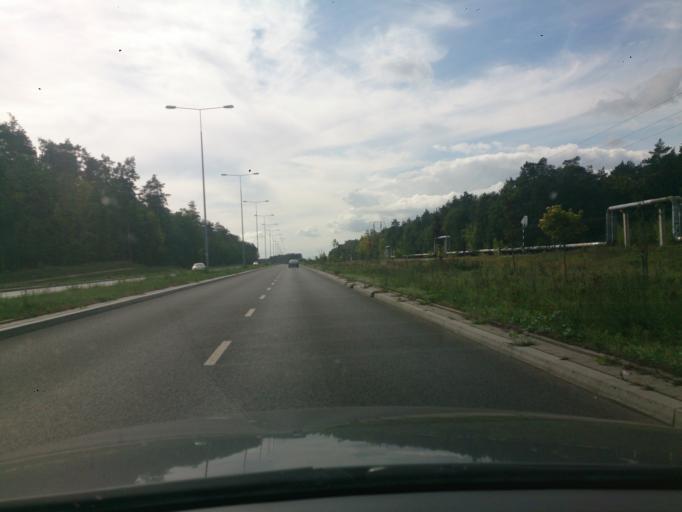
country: PL
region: Kujawsko-Pomorskie
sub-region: Grudziadz
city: Grudziadz
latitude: 53.4587
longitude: 18.7418
